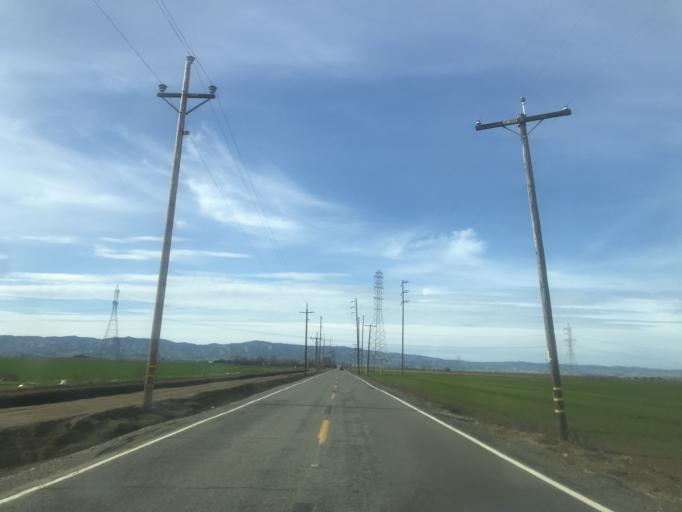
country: US
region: California
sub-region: Yolo County
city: Cottonwood
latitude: 38.6638
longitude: -121.9300
